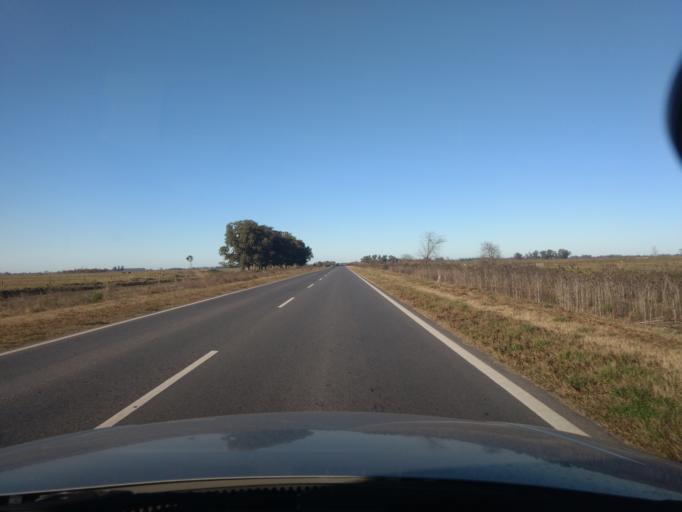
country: AR
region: Buenos Aires
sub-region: Partido de Navarro
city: Navarro
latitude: -34.8892
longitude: -59.2197
